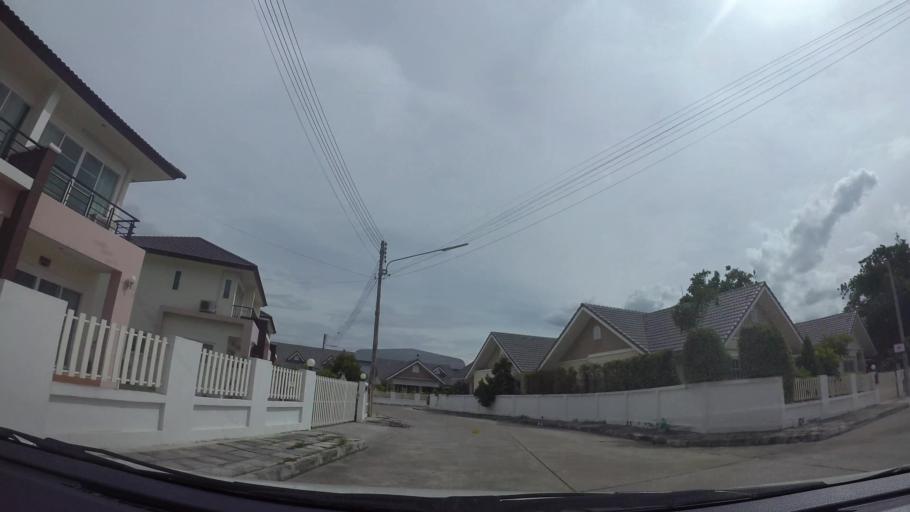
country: TH
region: Chiang Mai
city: Chiang Mai
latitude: 18.7460
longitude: 98.9769
